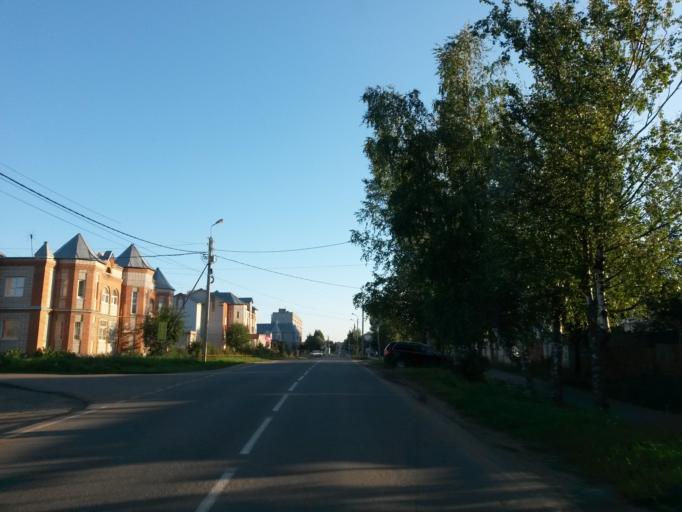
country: RU
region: Jaroslavl
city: Tutayev
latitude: 57.8709
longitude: 39.5219
